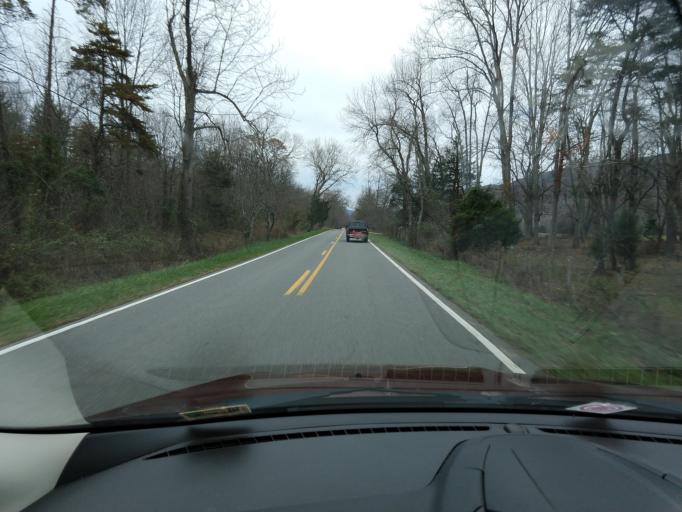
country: US
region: Virginia
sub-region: City of Covington
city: Covington
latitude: 37.7647
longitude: -80.1192
